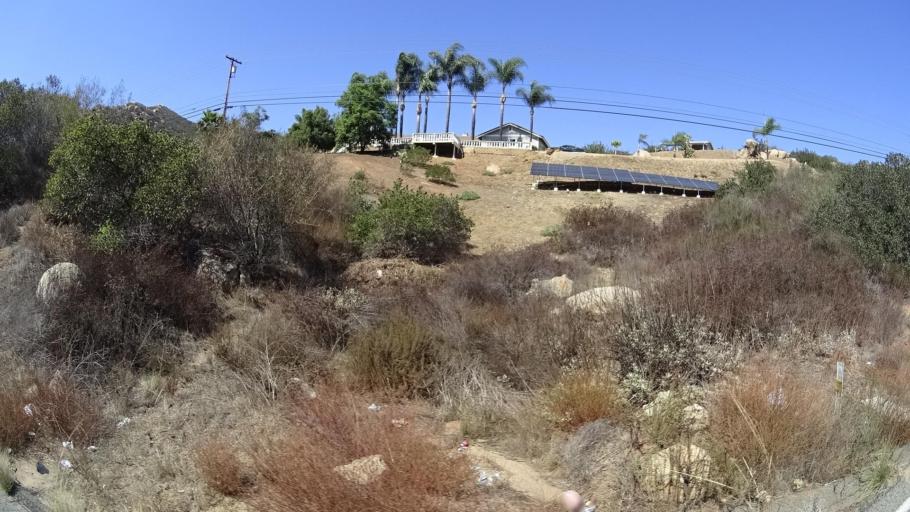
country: US
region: California
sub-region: San Diego County
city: Crest
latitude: 32.8104
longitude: -116.8791
